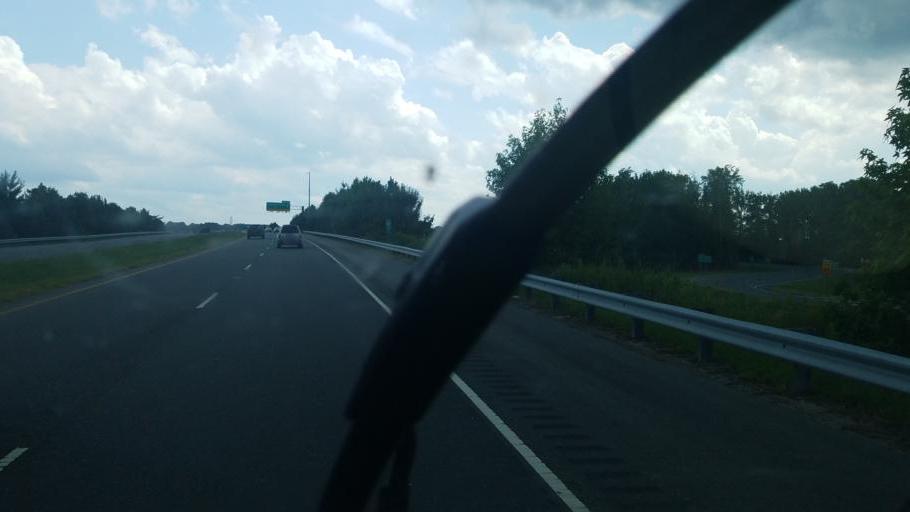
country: US
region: North Carolina
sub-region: Currituck County
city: Moyock
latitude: 36.6606
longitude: -76.2306
